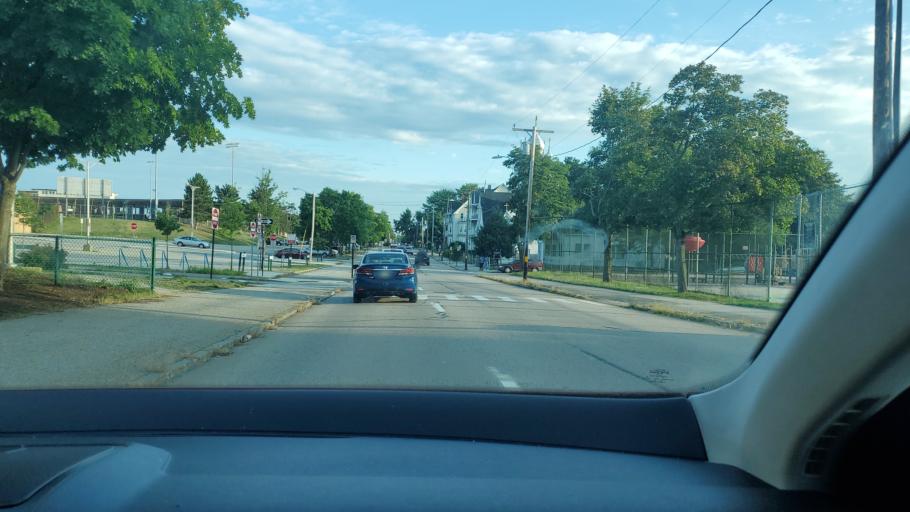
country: US
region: New Hampshire
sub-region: Hillsborough County
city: Manchester
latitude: 42.9842
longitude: -71.4553
